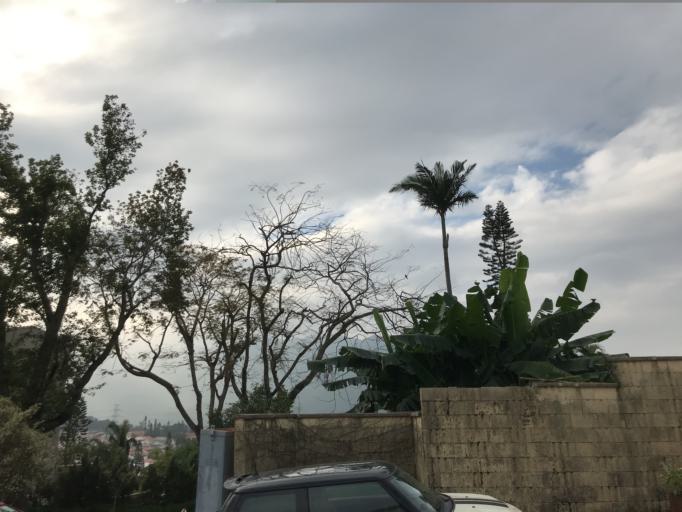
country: HK
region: Tai Po
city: Tai Po
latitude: 22.4635
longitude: 114.1586
